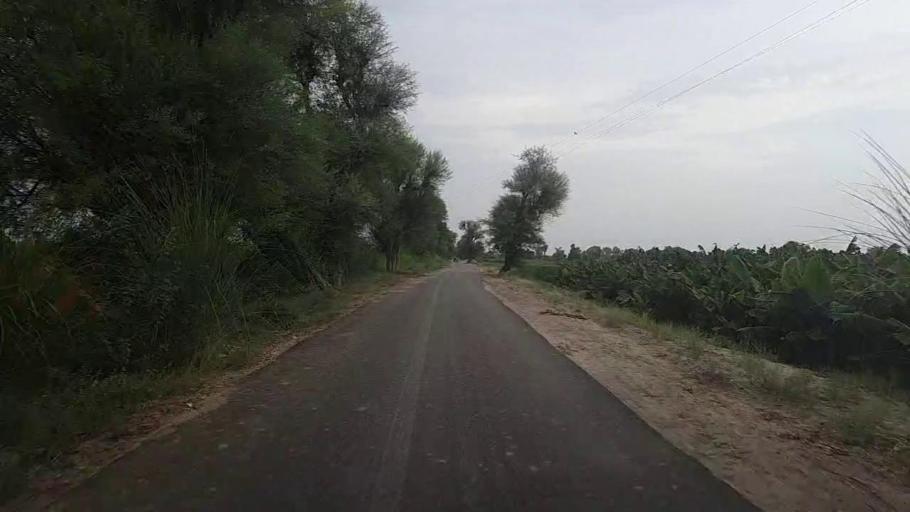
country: PK
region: Sindh
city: Karaundi
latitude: 26.9799
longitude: 68.3574
